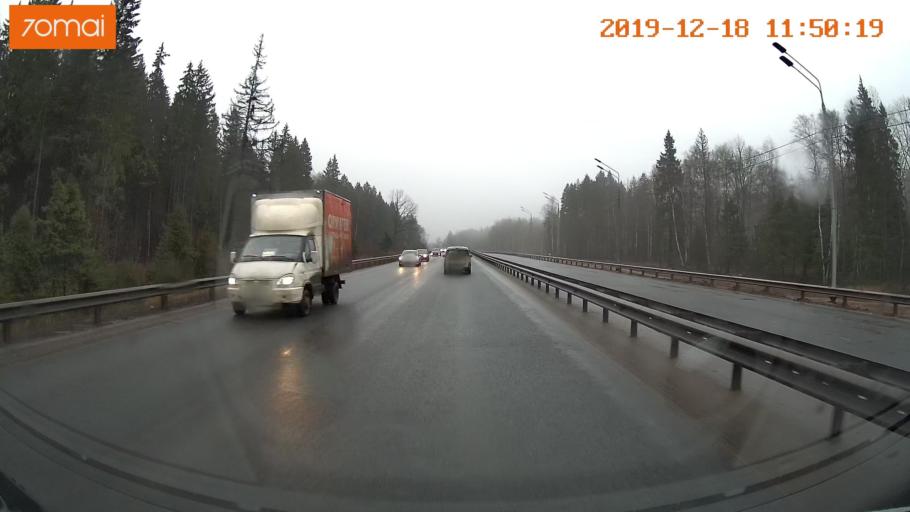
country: RU
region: Moskovskaya
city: Yershovo
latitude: 55.7848
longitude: 36.9178
